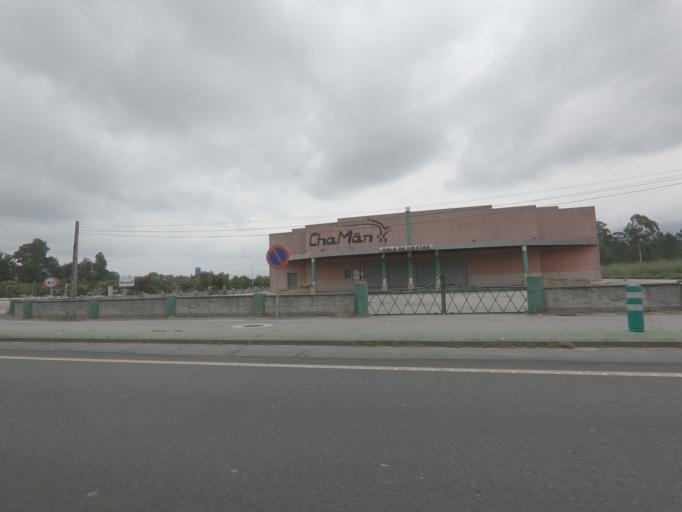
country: PT
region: Viana do Castelo
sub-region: Vila Nova de Cerveira
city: Vila Nova de Cerveira
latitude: 41.9579
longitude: -8.7644
